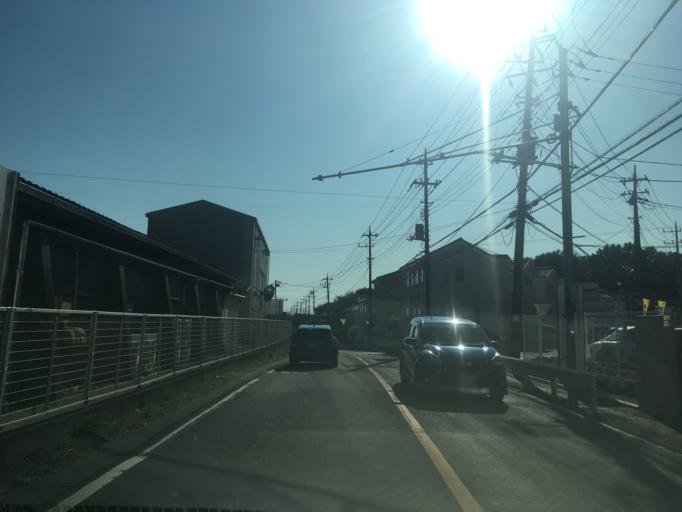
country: JP
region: Saitama
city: Kawagoe
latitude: 35.8899
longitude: 139.4779
